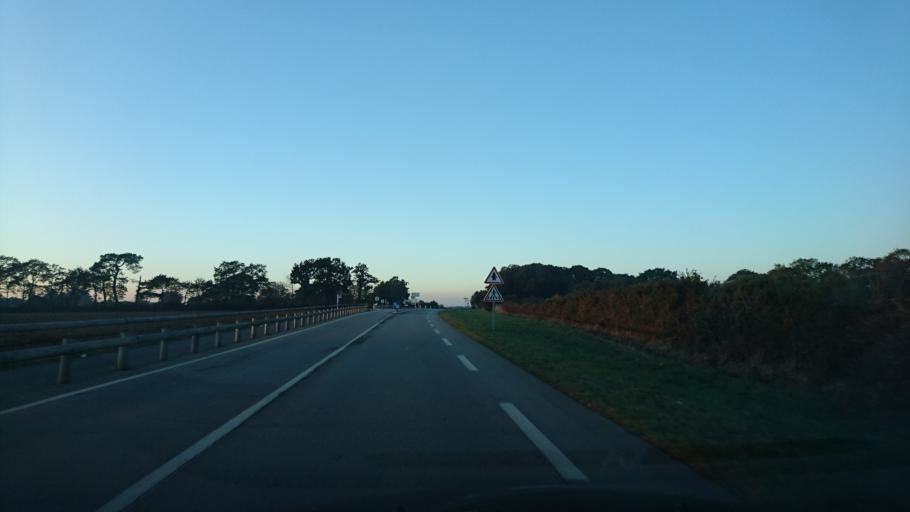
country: FR
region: Brittany
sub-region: Departement du Morbihan
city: Pluneret
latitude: 47.6586
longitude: -2.9640
